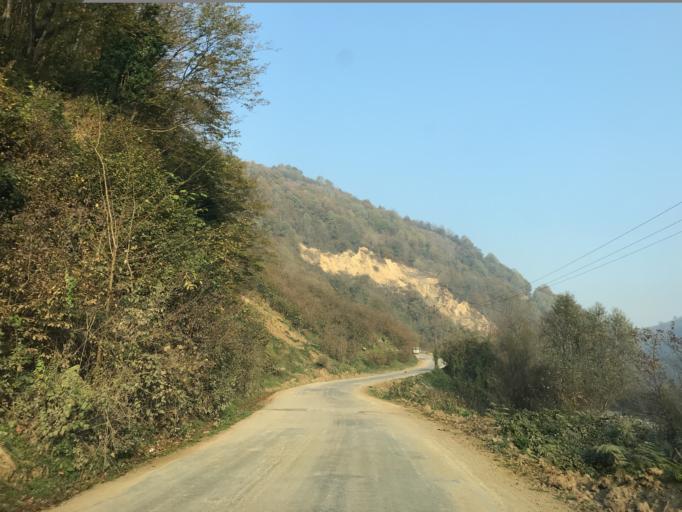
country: TR
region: Duzce
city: Cumayeri
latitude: 40.9196
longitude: 30.9295
